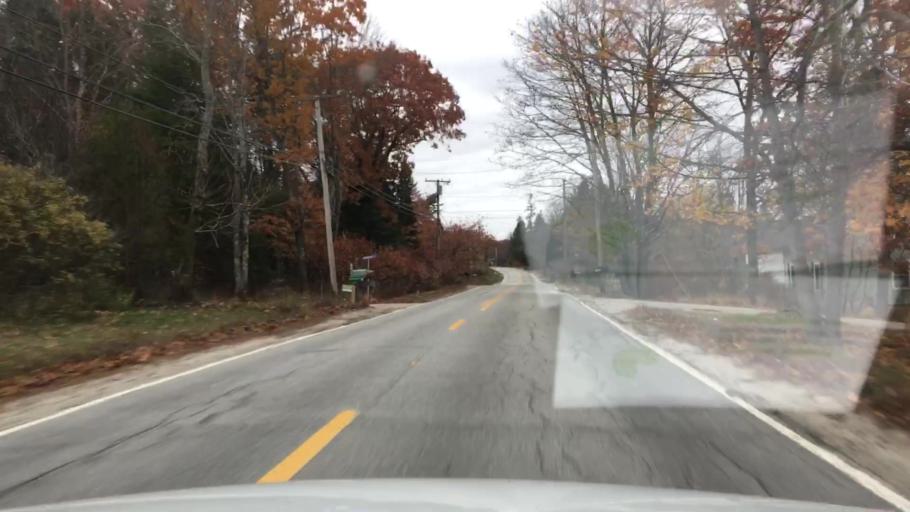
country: US
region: Maine
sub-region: Hancock County
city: Sedgwick
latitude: 44.3593
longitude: -68.5496
